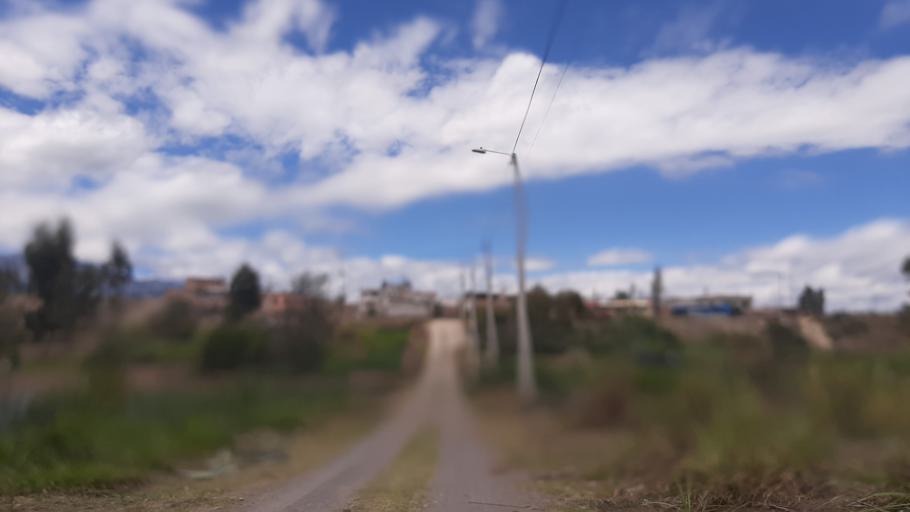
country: EC
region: Chimborazo
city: Riobamba
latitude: -1.6520
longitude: -78.6334
